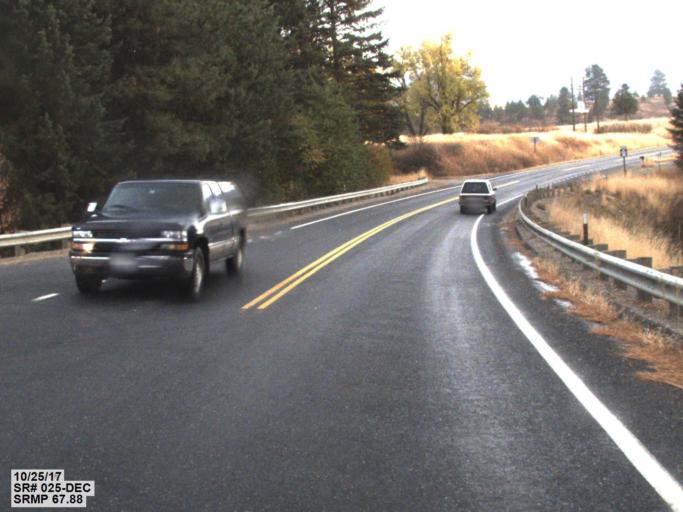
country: US
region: Washington
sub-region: Stevens County
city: Kettle Falls
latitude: 48.4510
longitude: -118.1729
